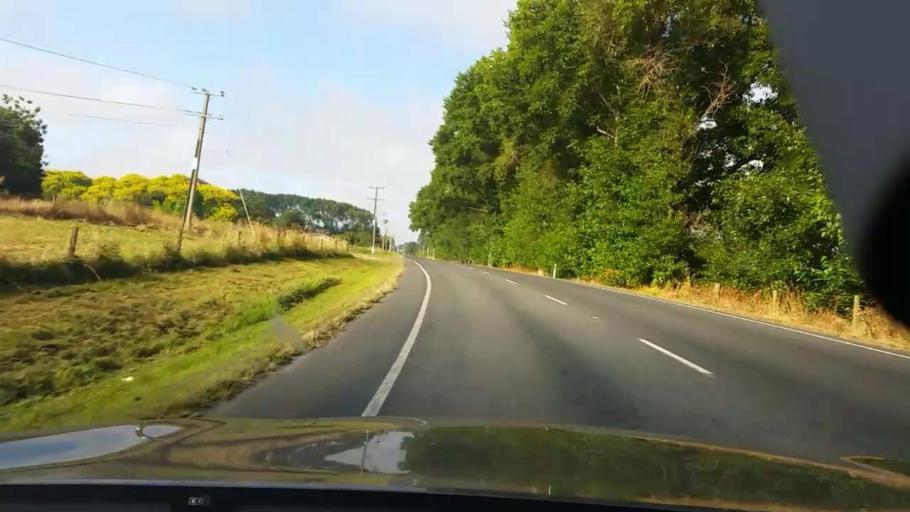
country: NZ
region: Waikato
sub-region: Hamilton City
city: Hamilton
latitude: -37.5984
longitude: 175.3540
